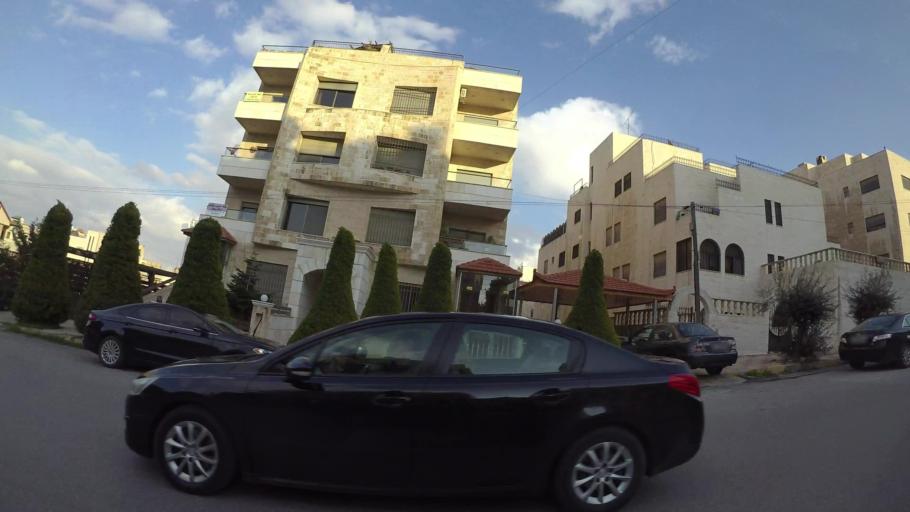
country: JO
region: Amman
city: Al Jubayhah
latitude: 31.9774
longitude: 35.8817
